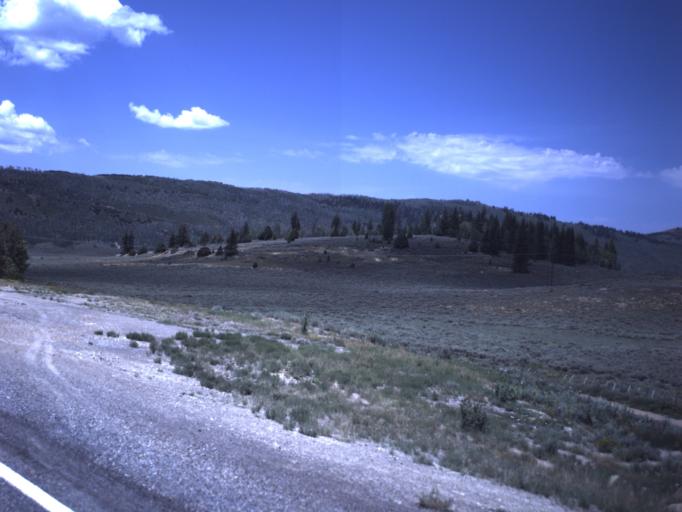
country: US
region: Utah
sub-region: Carbon County
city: Helper
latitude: 39.8646
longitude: -111.1189
